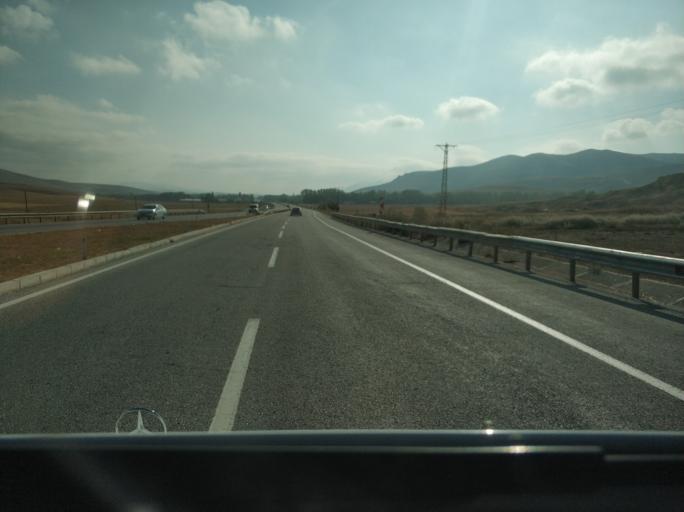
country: TR
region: Sivas
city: Yildizeli
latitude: 39.8362
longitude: 36.4466
